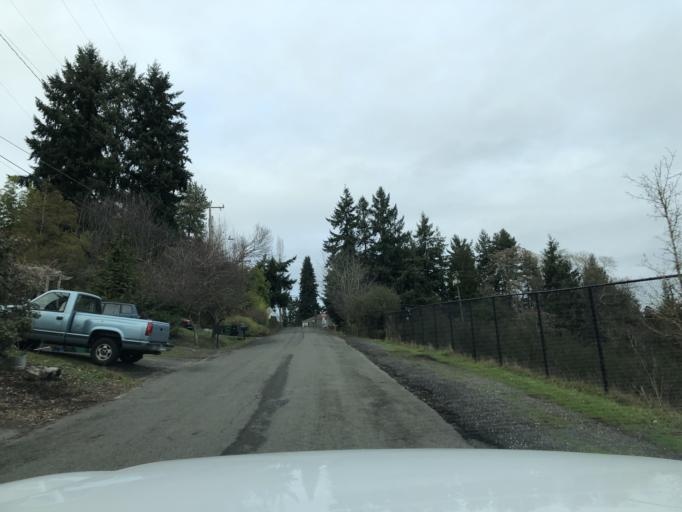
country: US
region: Washington
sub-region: King County
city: Lake Forest Park
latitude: 47.7110
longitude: -122.2948
